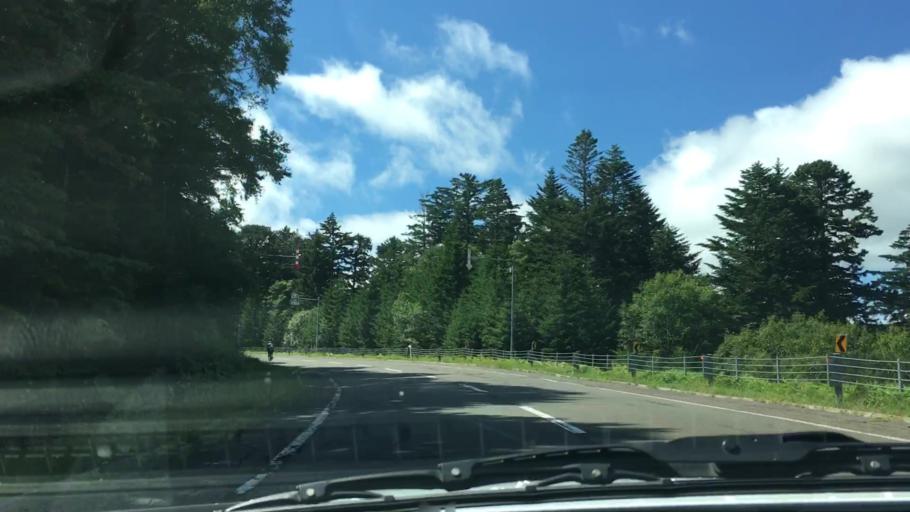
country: JP
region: Hokkaido
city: Kitami
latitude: 43.4431
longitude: 144.0134
